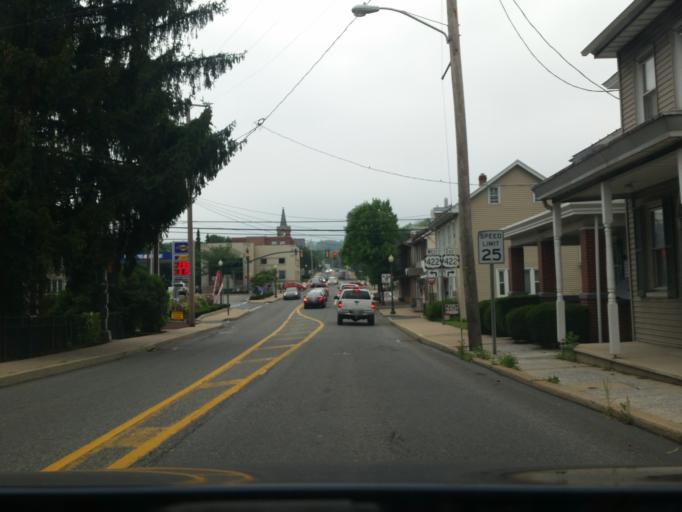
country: US
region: Pennsylvania
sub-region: Lebanon County
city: Annville
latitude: 40.3282
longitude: -76.5152
